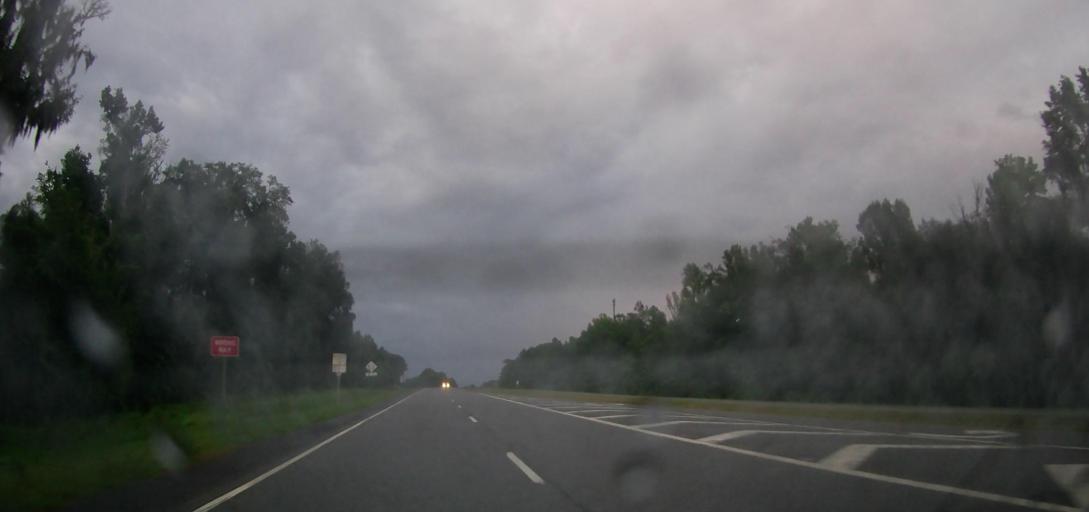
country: US
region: Georgia
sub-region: Lanier County
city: Lakeland
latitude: 30.9319
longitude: -83.0183
